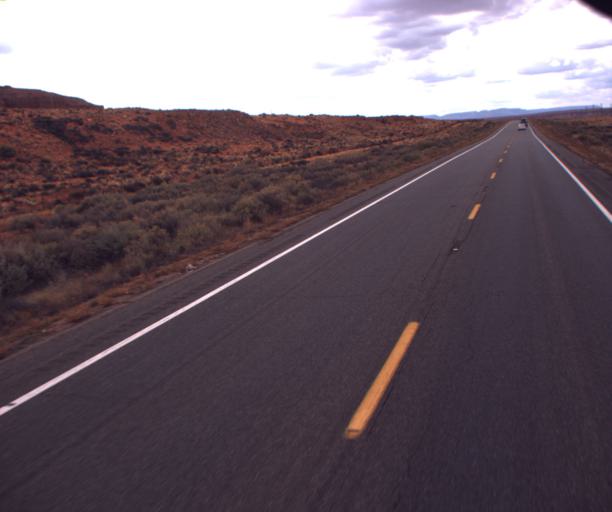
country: US
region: Arizona
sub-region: Navajo County
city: Kayenta
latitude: 36.7977
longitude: -109.9319
